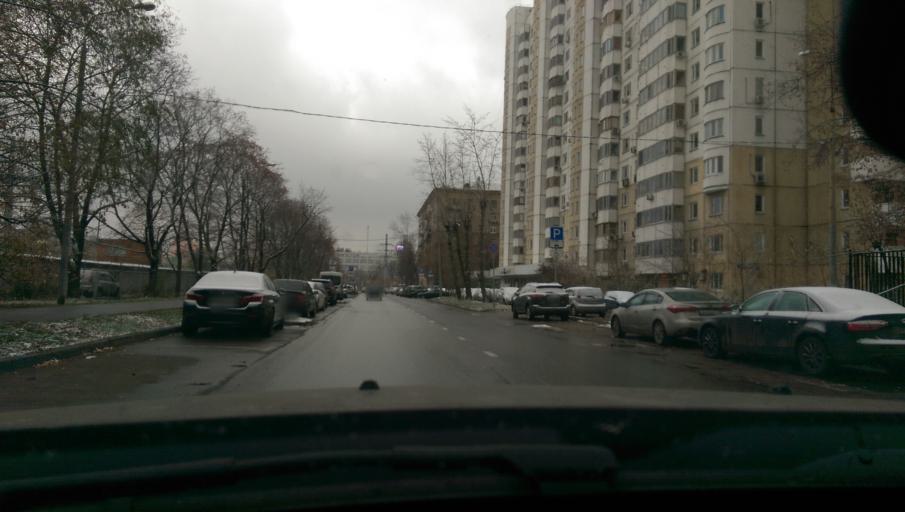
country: RU
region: Moskovskaya
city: Fili
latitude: 55.7412
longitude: 37.4935
